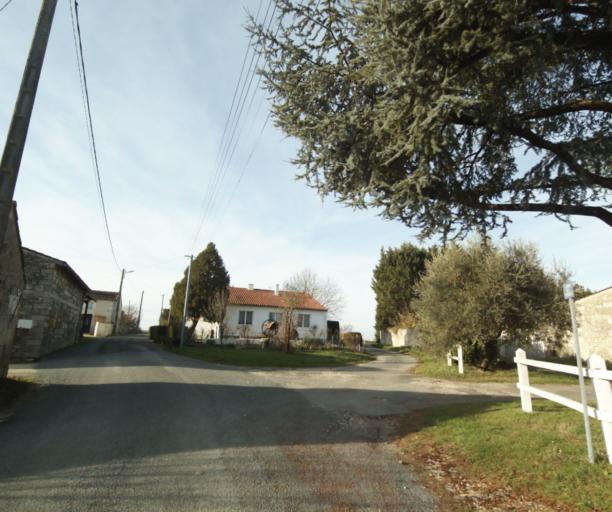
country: FR
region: Poitou-Charentes
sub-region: Departement de la Charente-Maritime
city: Chaniers
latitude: 45.7324
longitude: -0.5200
